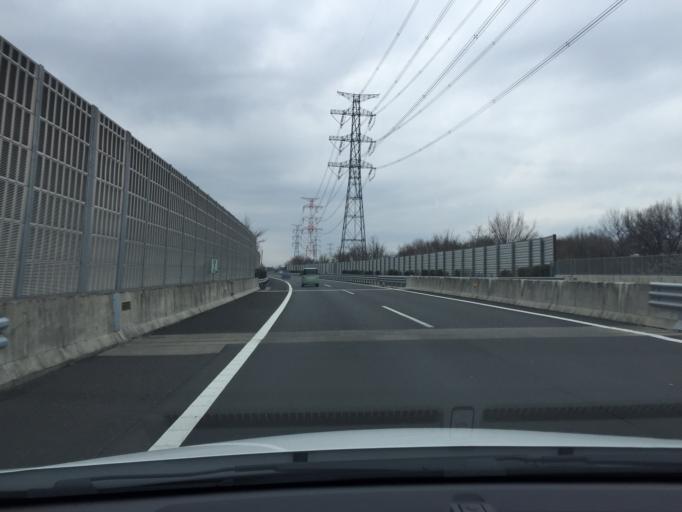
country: JP
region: Saitama
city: Sakado
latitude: 35.9579
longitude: 139.4311
